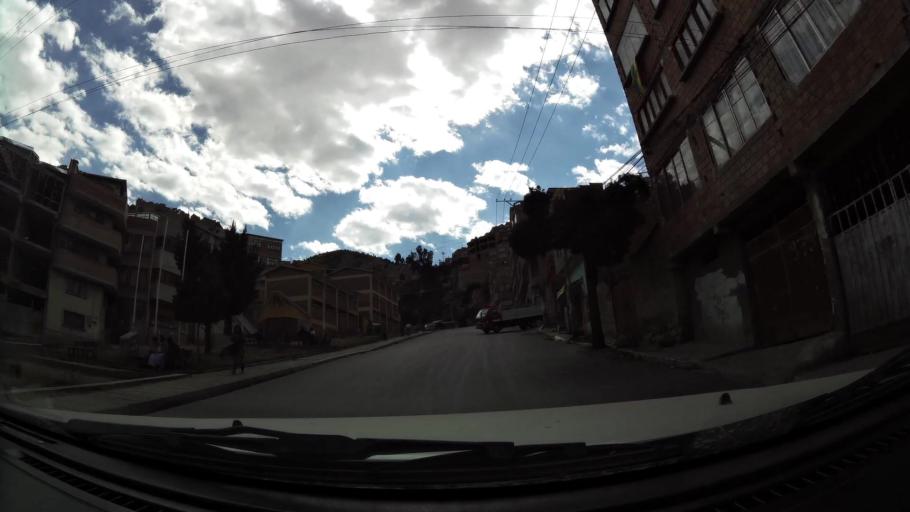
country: BO
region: La Paz
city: La Paz
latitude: -16.4762
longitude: -68.1244
